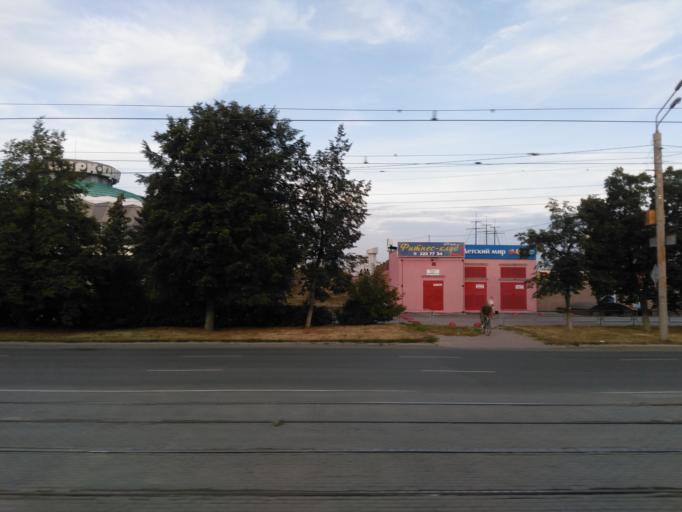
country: RU
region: Chelyabinsk
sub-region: Gorod Chelyabinsk
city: Chelyabinsk
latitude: 55.1719
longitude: 61.3998
